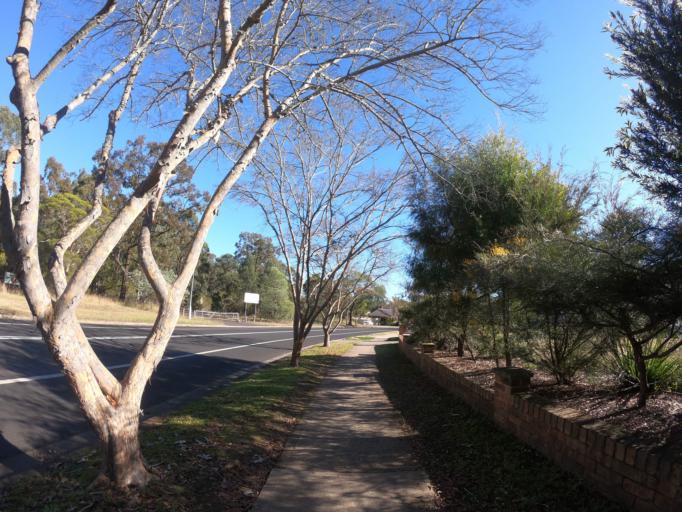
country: AU
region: New South Wales
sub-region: Hawkesbury
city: South Windsor
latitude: -33.6401
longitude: 150.7910
